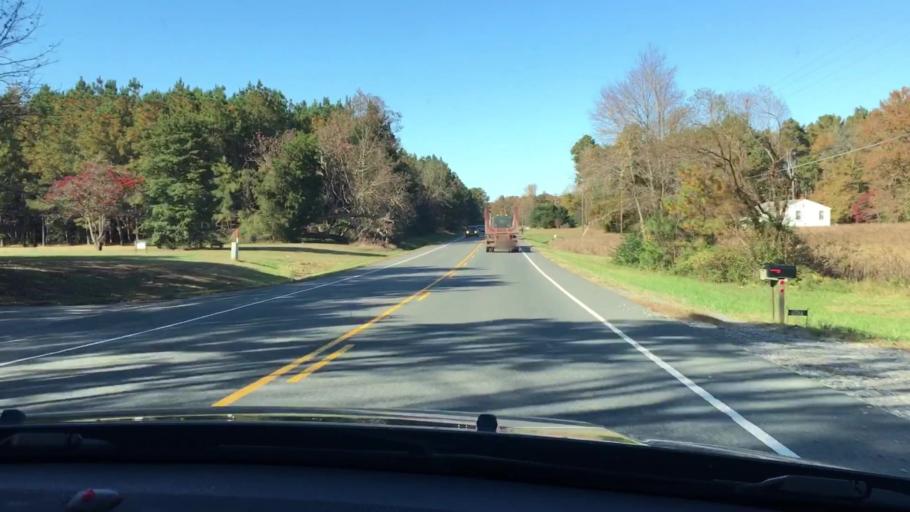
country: US
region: Virginia
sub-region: King William County
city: Central Garage
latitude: 37.7672
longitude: -77.1528
